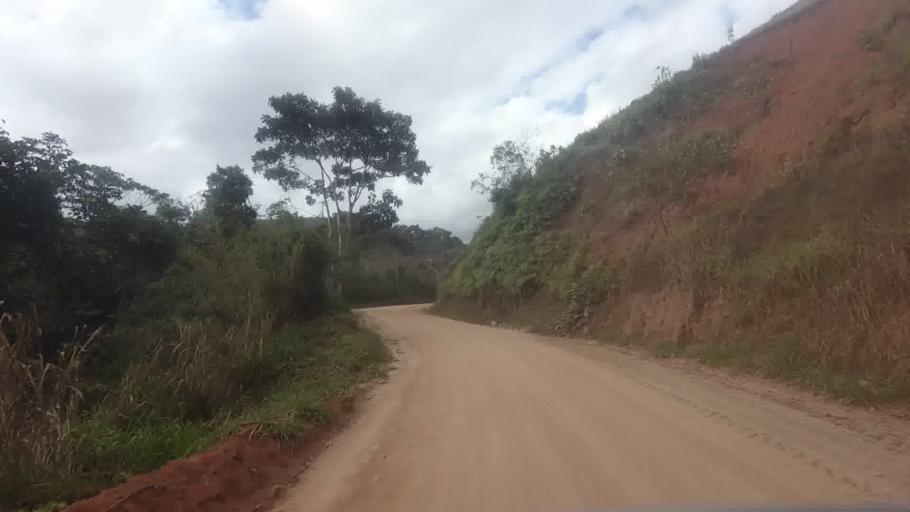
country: BR
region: Espirito Santo
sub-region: Mimoso Do Sul
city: Mimoso do Sul
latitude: -20.9648
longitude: -41.4465
